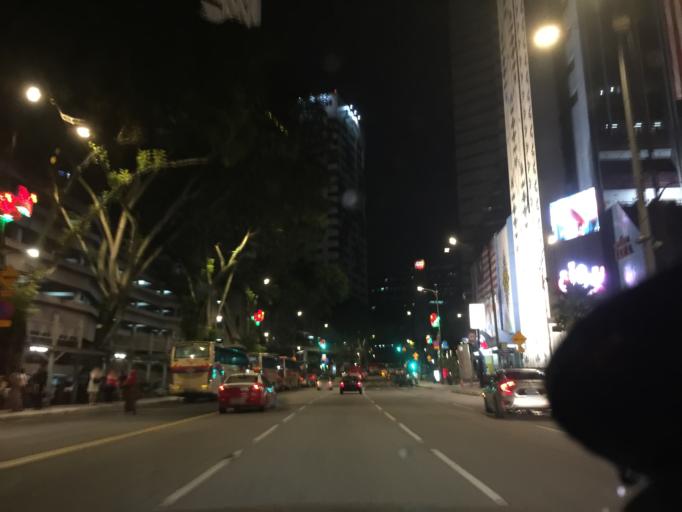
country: MY
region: Kuala Lumpur
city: Kuala Lumpur
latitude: 3.1573
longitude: 101.6948
